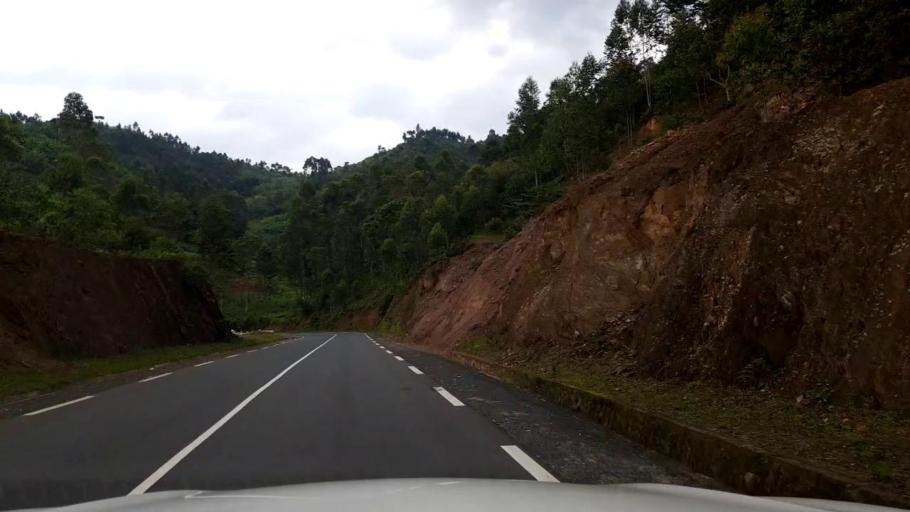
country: RW
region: Western Province
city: Kibuye
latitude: -1.9061
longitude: 29.3621
